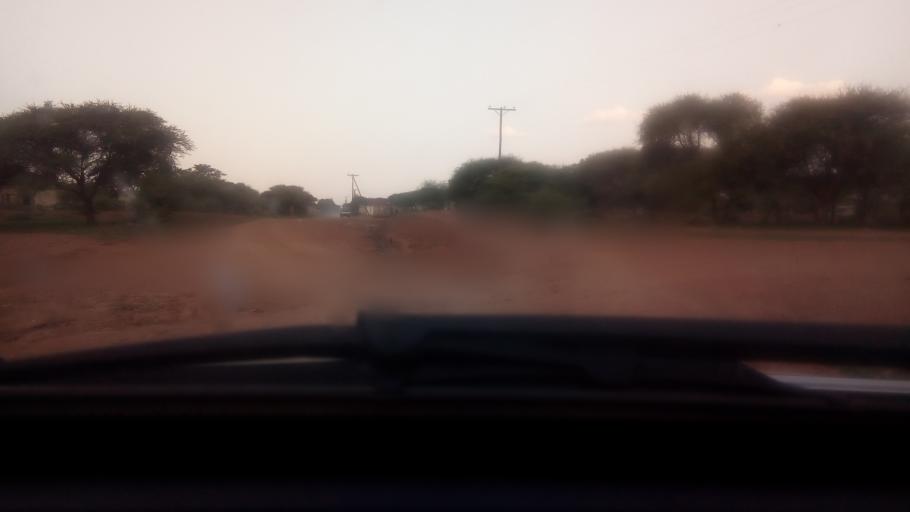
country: BW
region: Kgatleng
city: Bokaa
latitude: -24.4309
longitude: 26.0072
